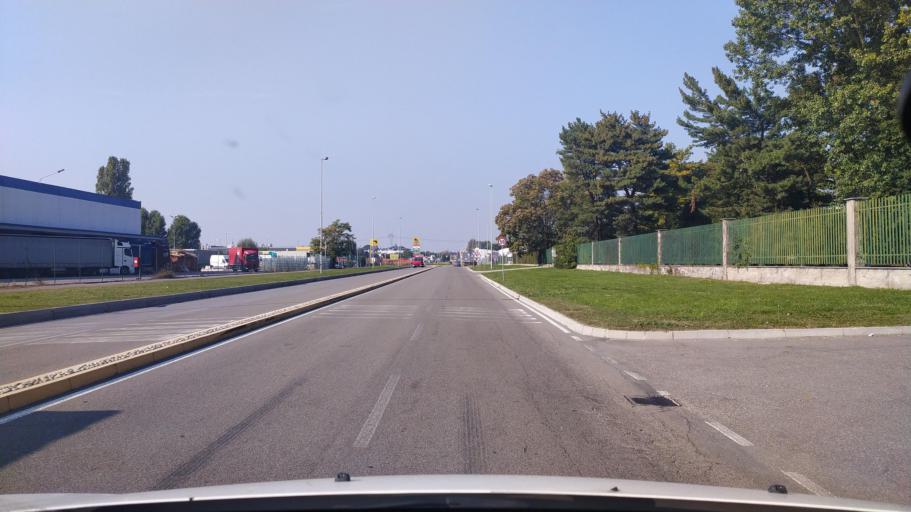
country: IT
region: Lombardy
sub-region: Citta metropolitana di Milano
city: Cusago
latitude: 45.4387
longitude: 9.0452
